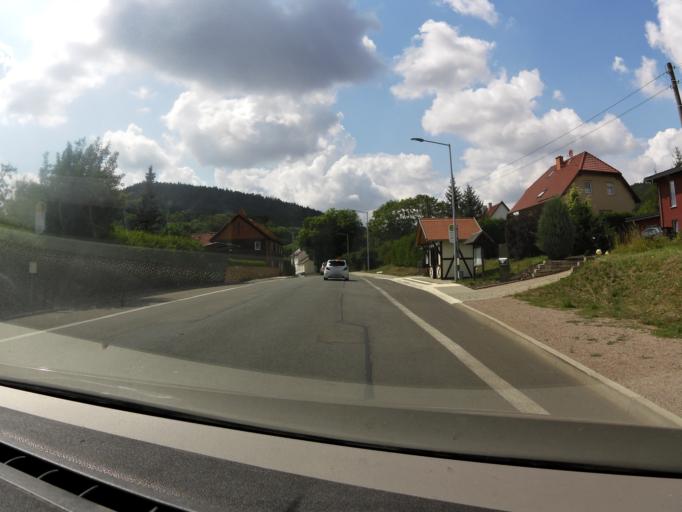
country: DE
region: Thuringia
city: Plaue
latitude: 50.7986
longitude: 10.9156
